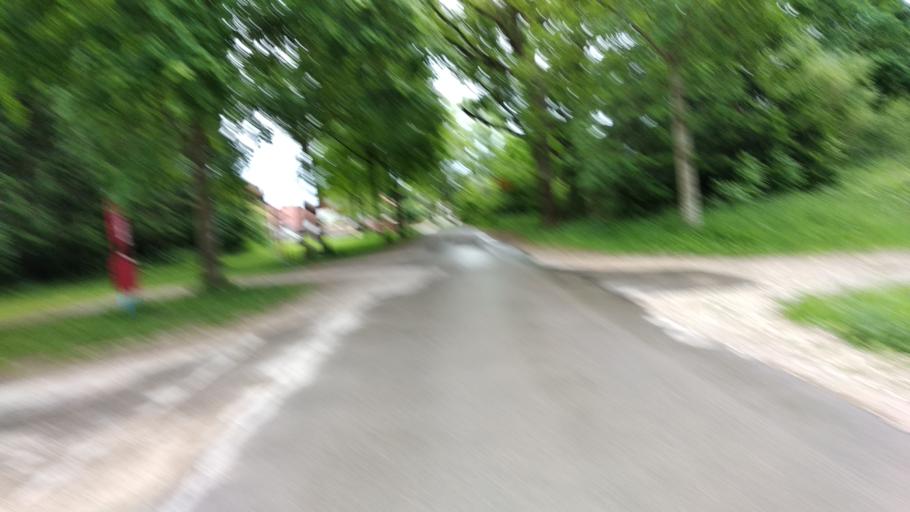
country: DE
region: Baden-Wuerttemberg
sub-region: Tuebingen Region
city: Aitrach
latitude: 47.9445
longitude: 10.0907
